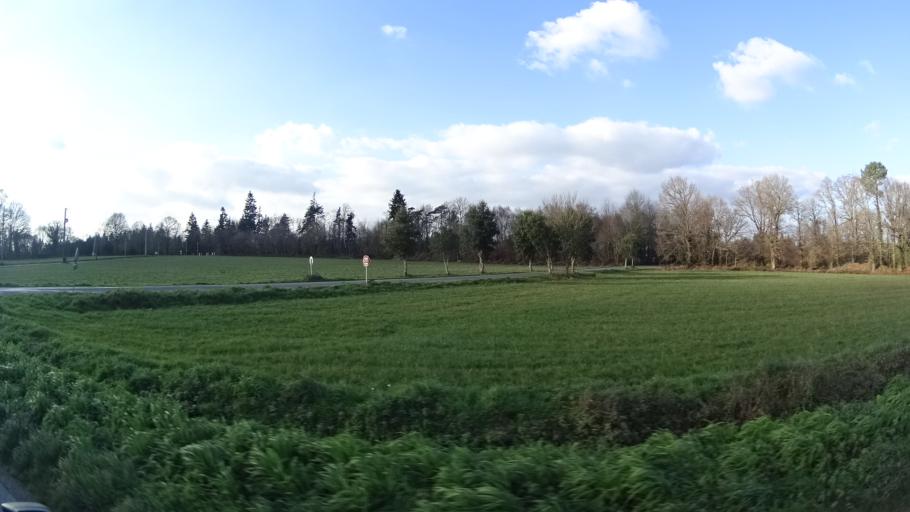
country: FR
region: Pays de la Loire
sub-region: Departement de la Loire-Atlantique
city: Guemene-Penfao
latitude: 47.6203
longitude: -1.8349
